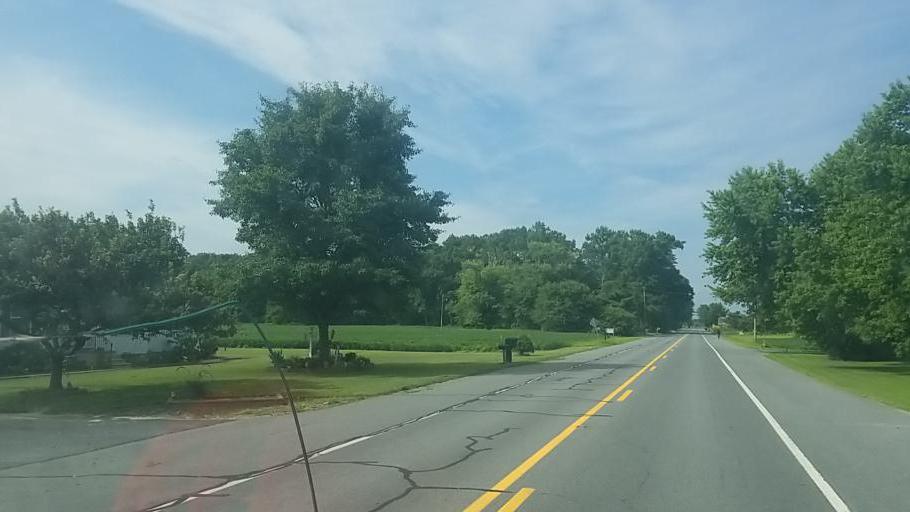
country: US
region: Delaware
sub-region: Sussex County
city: Long Neck
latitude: 38.5404
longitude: -75.1816
